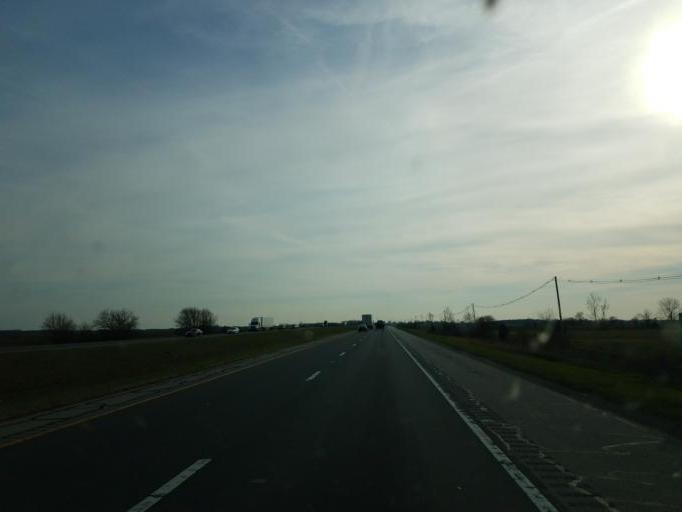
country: US
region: Ohio
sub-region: Fayette County
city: Jeffersonville
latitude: 39.6805
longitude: -83.4875
